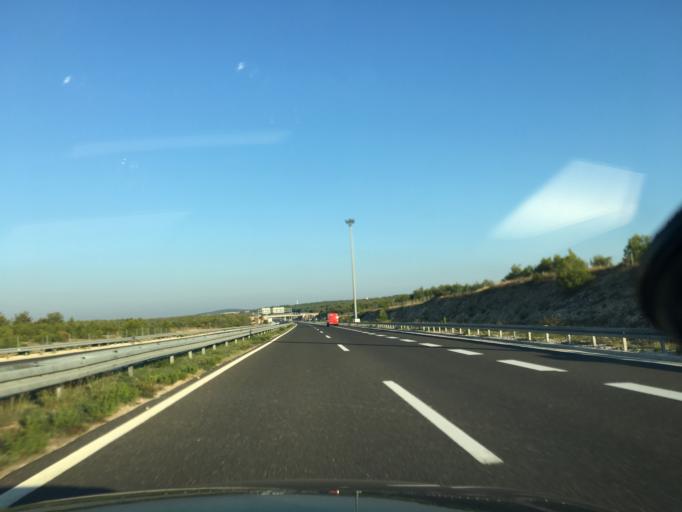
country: HR
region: Sibensko-Kniniska
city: Zaton
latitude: 43.8381
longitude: 15.8850
